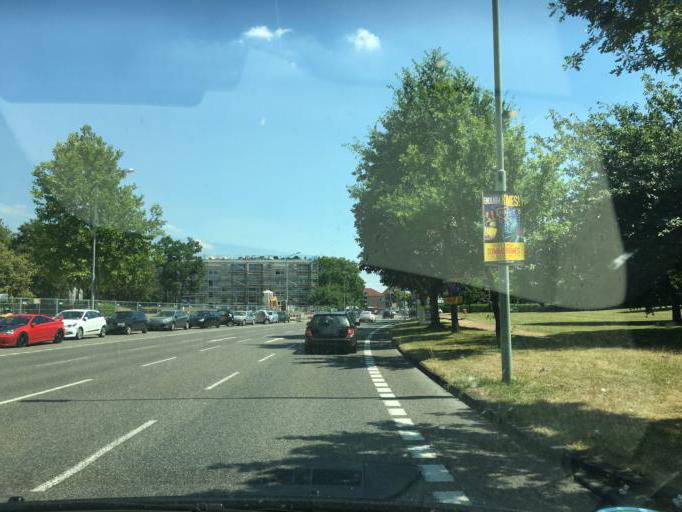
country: DE
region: North Rhine-Westphalia
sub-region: Regierungsbezirk Koln
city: Eschweiler
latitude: 50.8214
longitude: 6.2585
